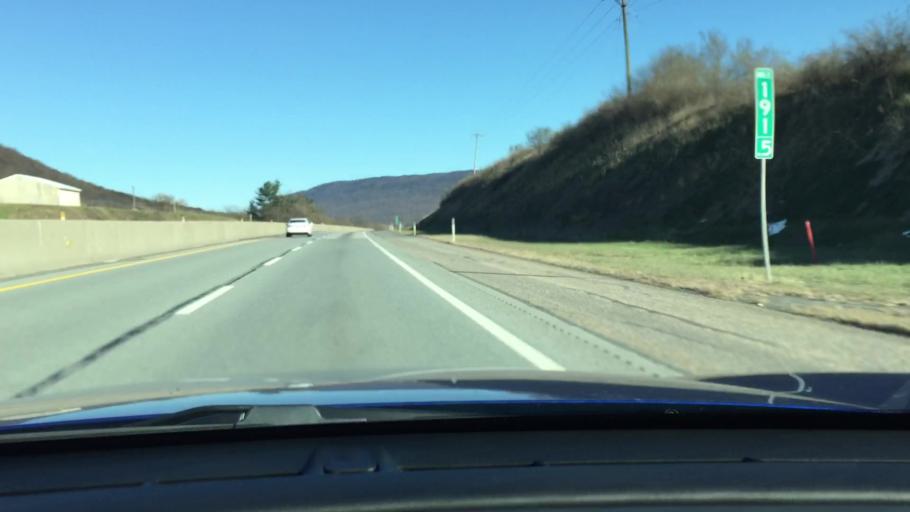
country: US
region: Pennsylvania
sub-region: Franklin County
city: Doylestown
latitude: 40.1224
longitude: -77.7720
